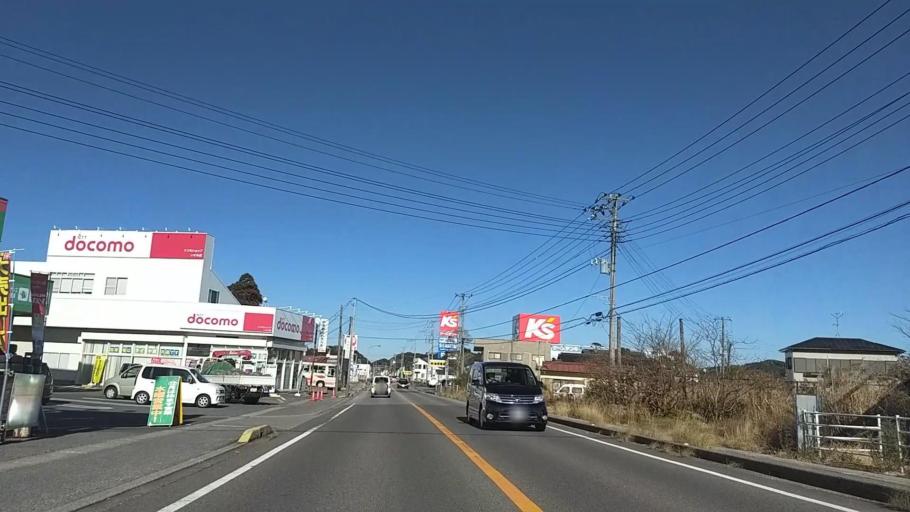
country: JP
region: Chiba
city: Ohara
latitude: 35.3003
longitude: 140.3978
